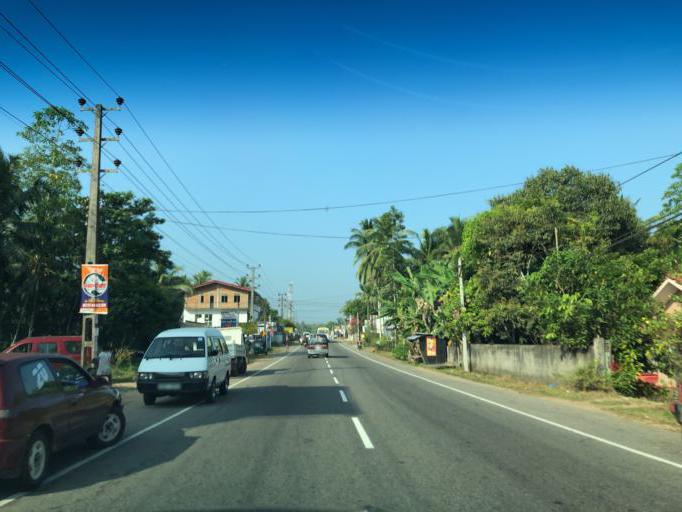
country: LK
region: Western
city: Horana South
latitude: 6.7245
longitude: 80.0921
